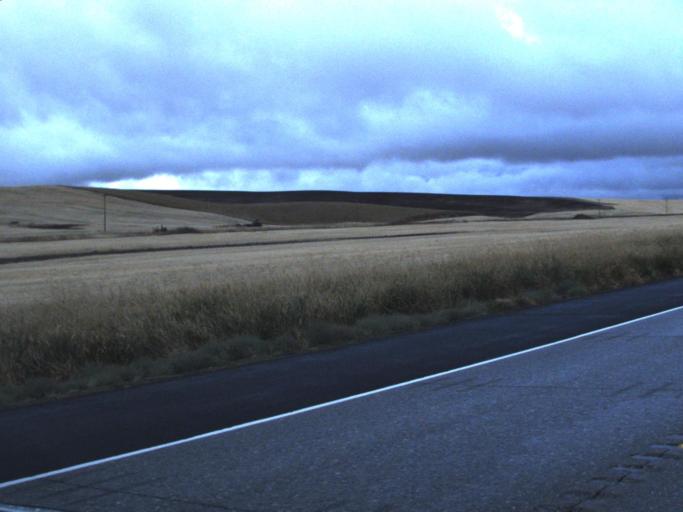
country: US
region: Washington
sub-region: Whitman County
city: Colfax
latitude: 47.0756
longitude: -117.3831
